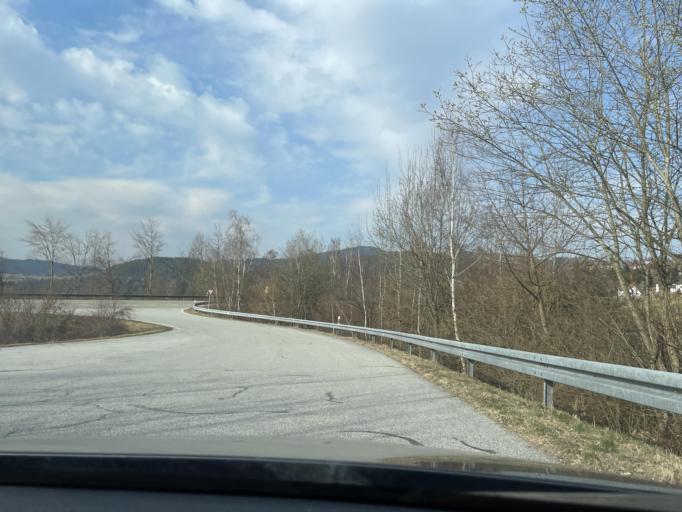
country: DE
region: Bavaria
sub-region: Lower Bavaria
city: Viechtach
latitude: 49.0824
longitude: 12.8997
